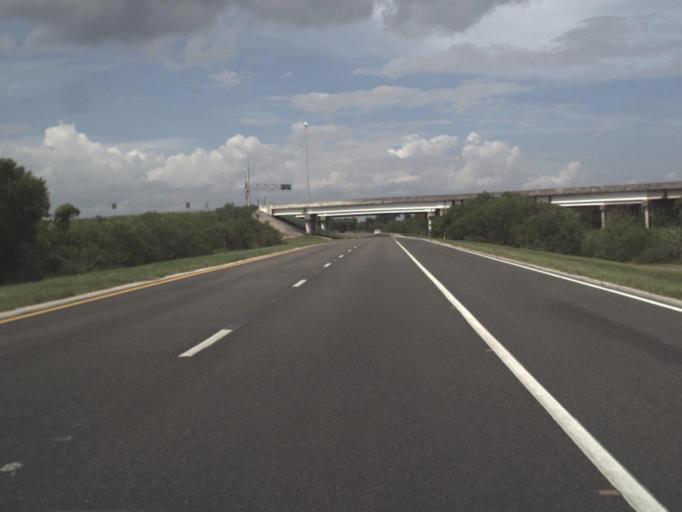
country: US
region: Florida
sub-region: Manatee County
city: Memphis
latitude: 27.5797
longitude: -82.5778
